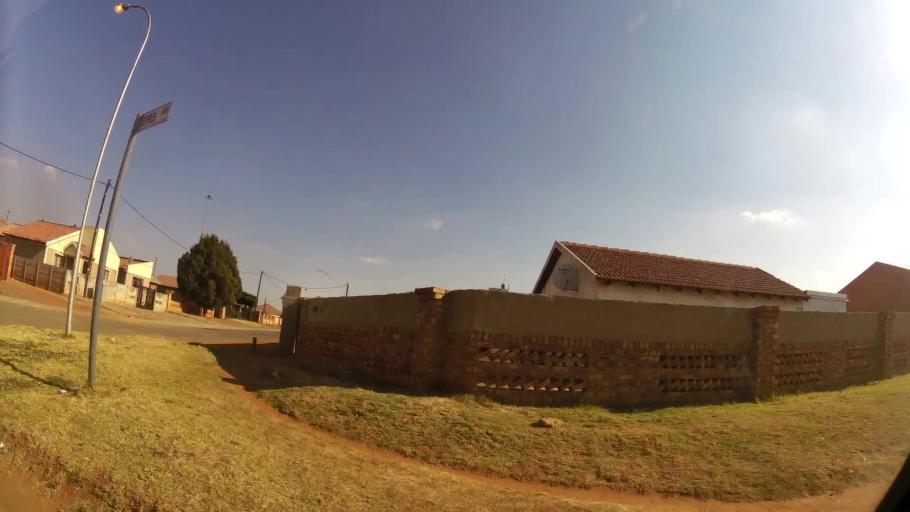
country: ZA
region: Gauteng
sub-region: Ekurhuleni Metropolitan Municipality
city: Benoni
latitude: -26.2279
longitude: 28.3243
